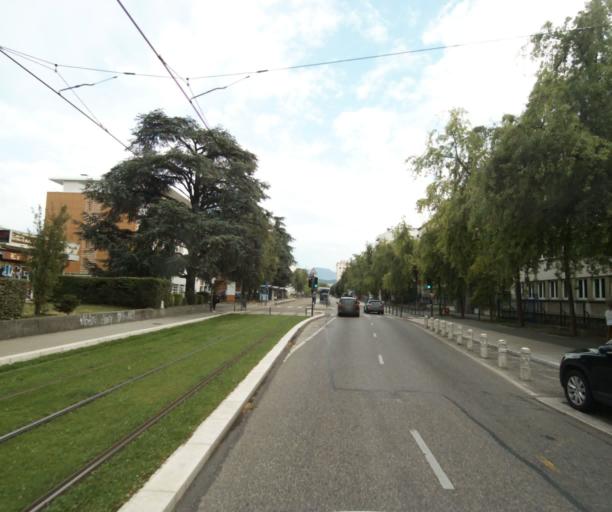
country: FR
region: Rhone-Alpes
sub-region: Departement de l'Isere
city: Grenoble
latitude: 45.1796
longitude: 5.7317
